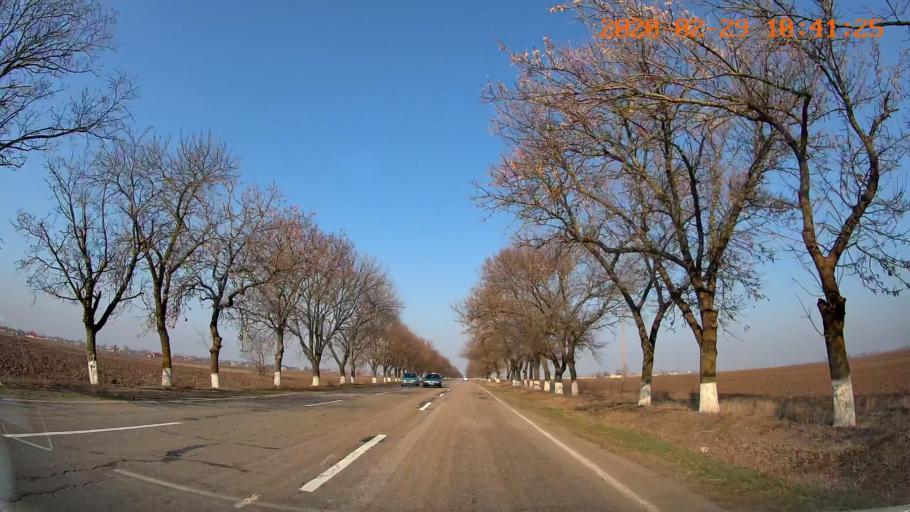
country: MD
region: Telenesti
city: Grigoriopol
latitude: 47.0422
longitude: 29.4255
